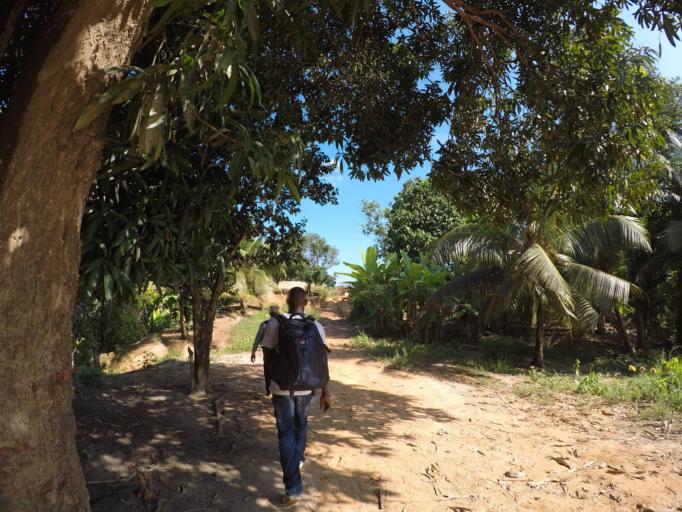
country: TZ
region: Pemba South
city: Mtambile
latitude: -5.3856
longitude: 39.7239
